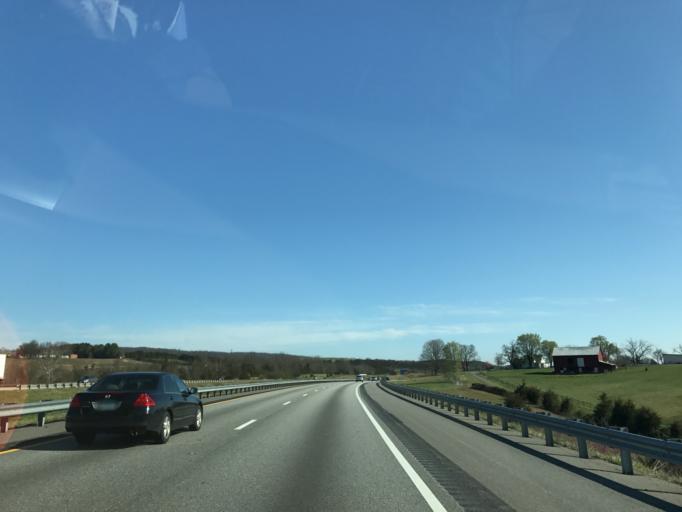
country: US
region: Virginia
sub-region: Augusta County
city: Verona
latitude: 38.2123
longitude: -78.9914
